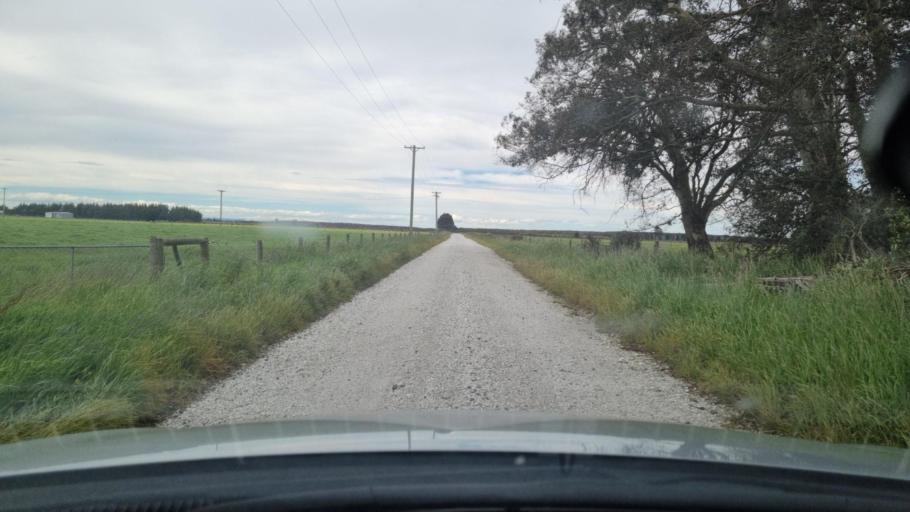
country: NZ
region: Southland
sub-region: Invercargill City
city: Invercargill
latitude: -46.5066
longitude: 168.4388
